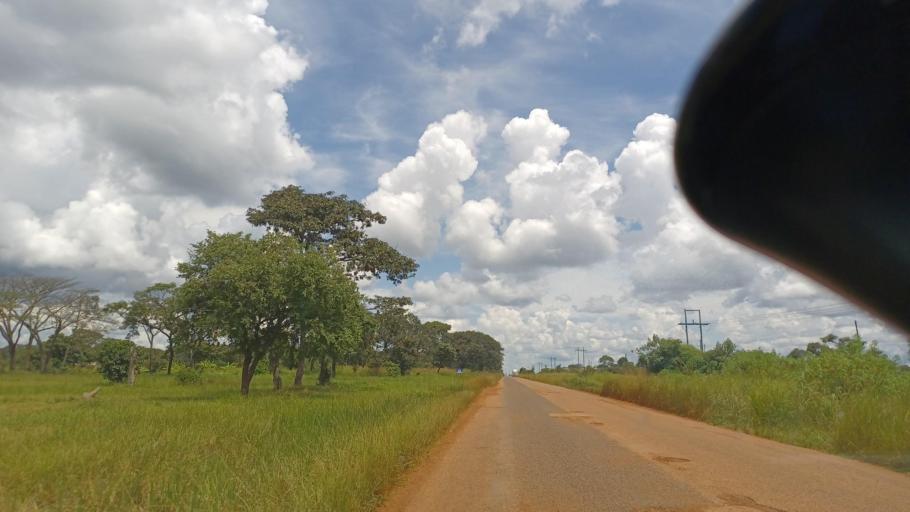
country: ZM
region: North-Western
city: Solwezi
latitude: -12.4887
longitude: 26.1918
